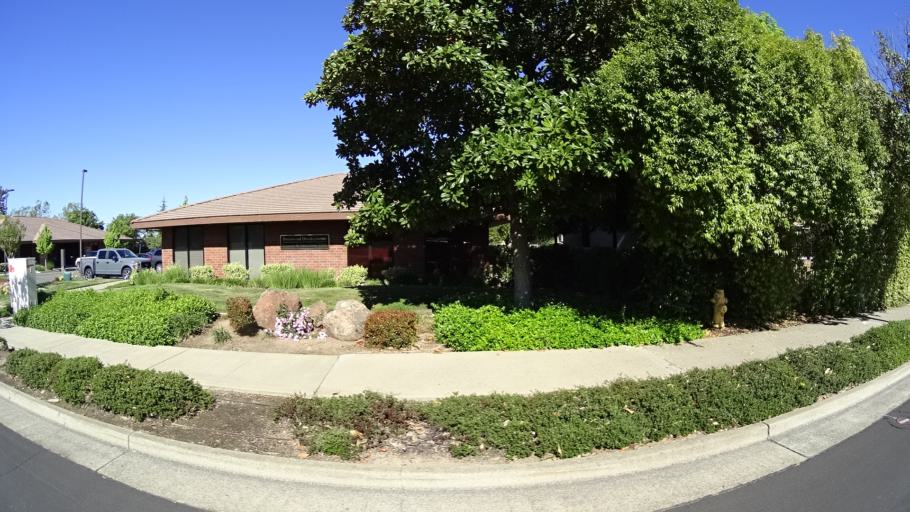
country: US
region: California
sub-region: Placer County
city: Rocklin
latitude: 38.7989
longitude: -121.2625
